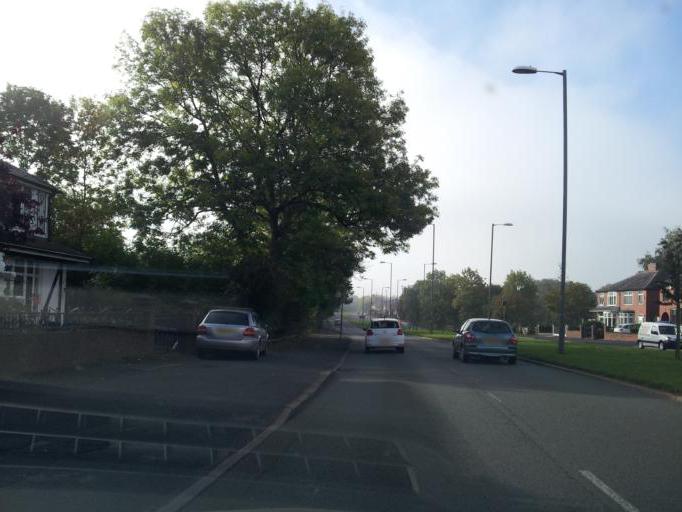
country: GB
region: England
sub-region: Manchester
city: Failsworth
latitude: 53.5148
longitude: -2.1697
